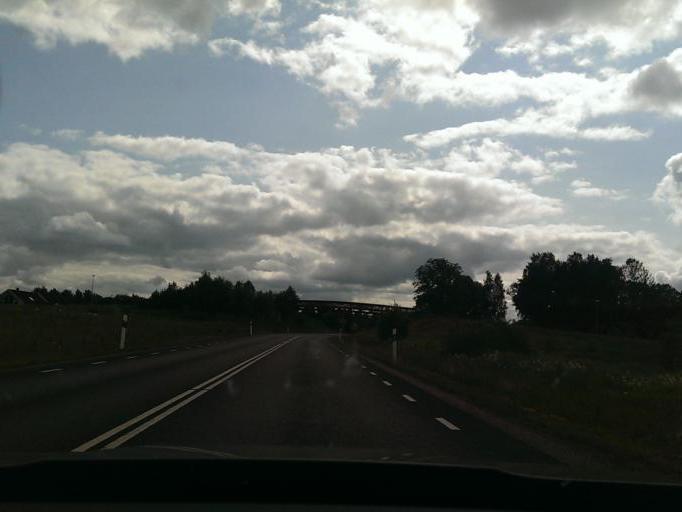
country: SE
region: Joenkoeping
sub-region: Varnamo Kommun
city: Varnamo
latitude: 57.1952
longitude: 14.0153
